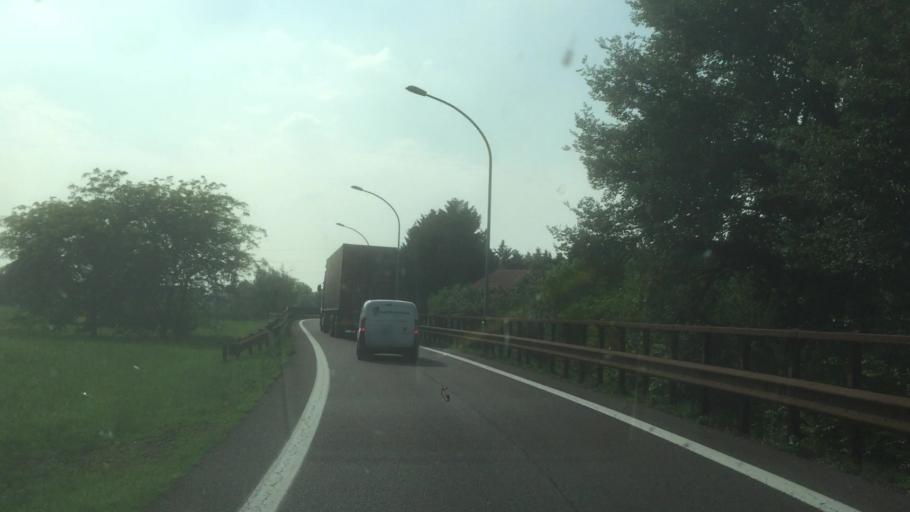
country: IT
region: Lombardy
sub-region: Provincia di Mantova
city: Stradella
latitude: 45.1692
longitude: 10.8591
